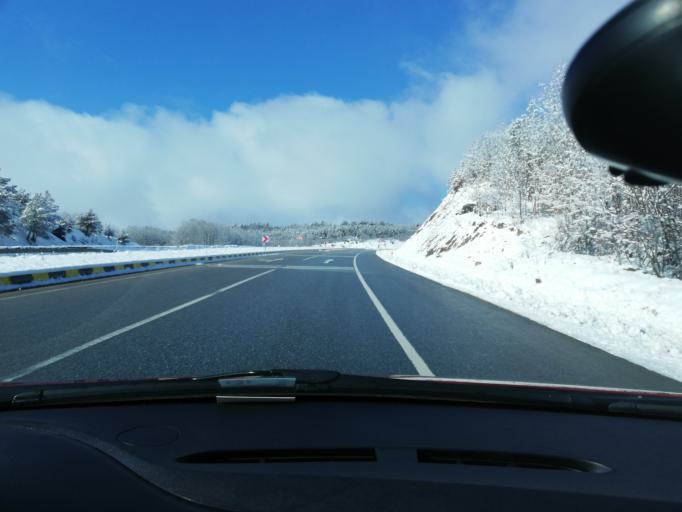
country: TR
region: Kastamonu
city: Kuzyaka
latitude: 41.3361
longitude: 33.6411
